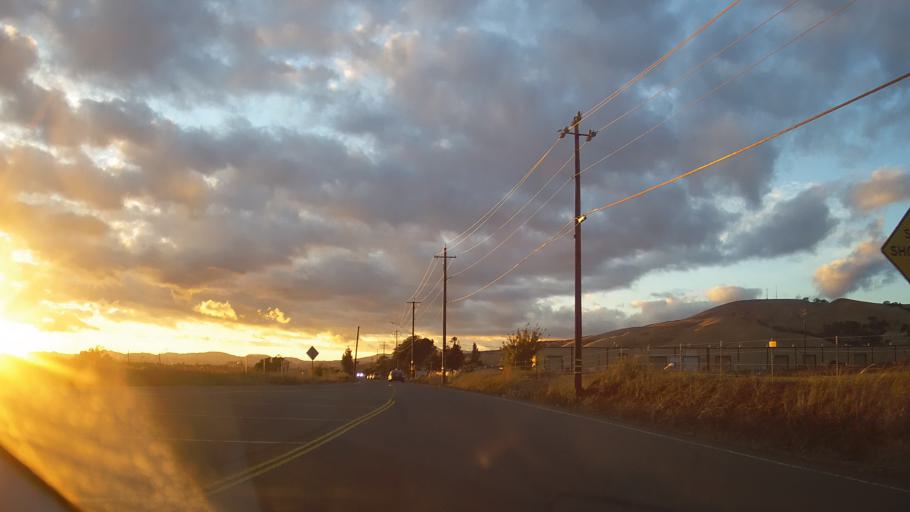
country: US
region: California
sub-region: Solano County
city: Vacaville
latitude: 38.2872
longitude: -121.9726
